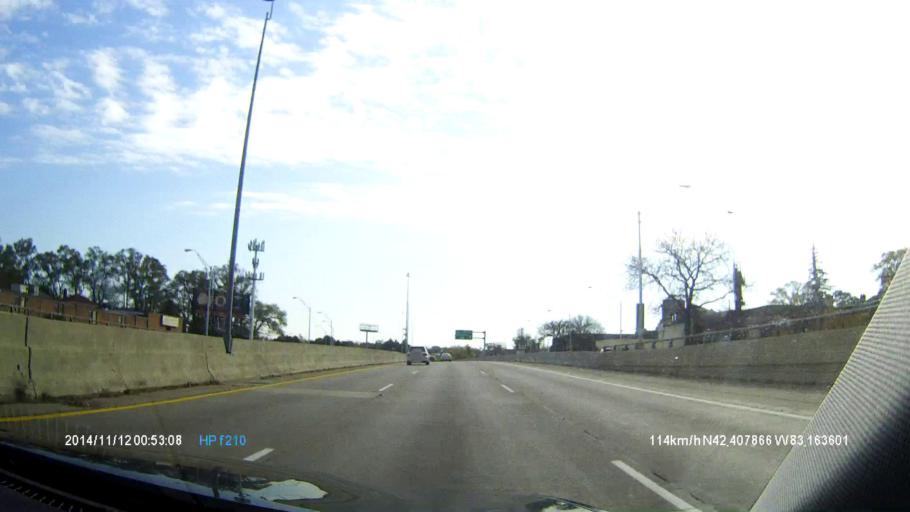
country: US
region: Michigan
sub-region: Oakland County
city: Oak Park
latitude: 42.4078
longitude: -83.1636
